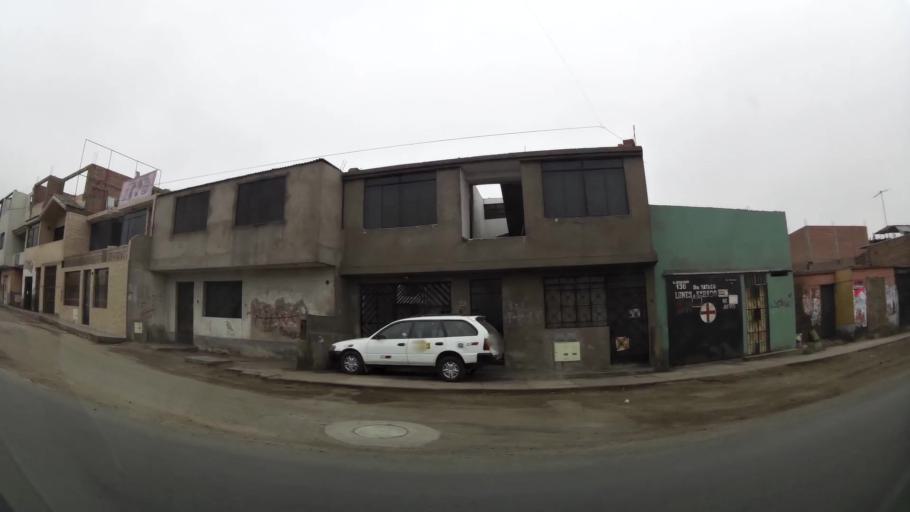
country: PE
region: Lima
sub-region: Lima
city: Urb. Santo Domingo
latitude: -11.9169
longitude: -77.0386
